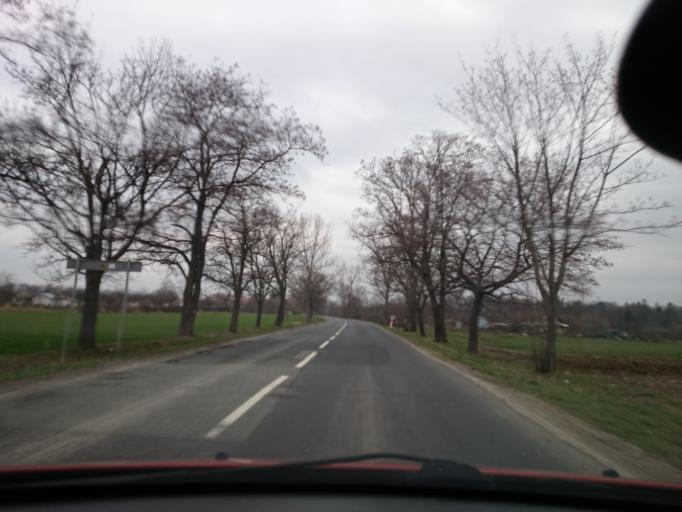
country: PL
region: Opole Voivodeship
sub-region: Powiat nyski
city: Paczkow
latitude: 50.4599
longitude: 17.0263
